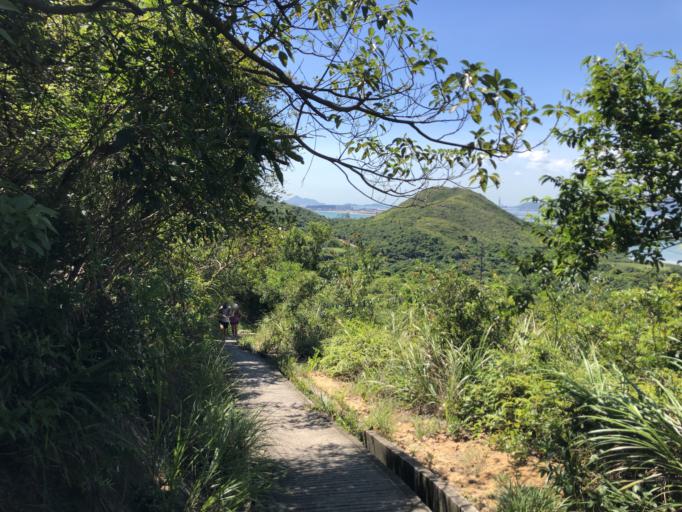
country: HK
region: Tuen Mun
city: Tuen Mun
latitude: 22.2875
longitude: 113.9816
